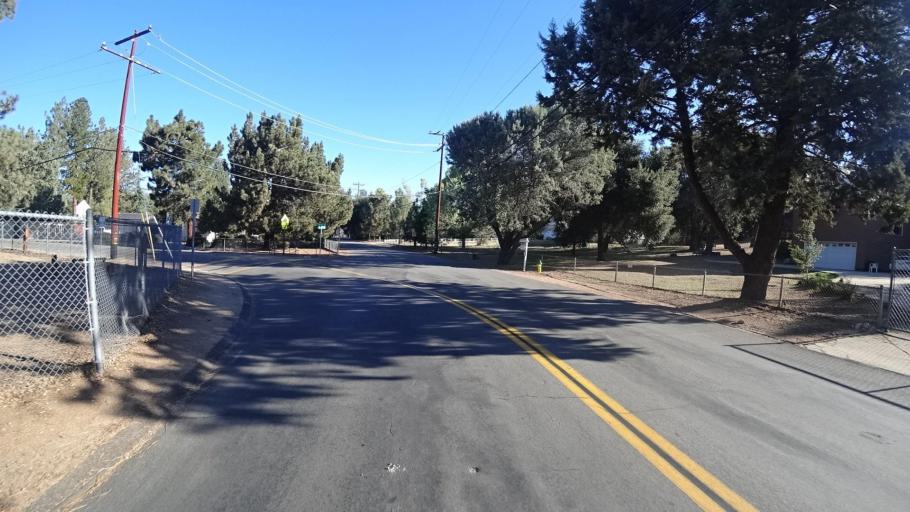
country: US
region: California
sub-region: San Diego County
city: Pine Valley
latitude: 32.8199
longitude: -116.5253
